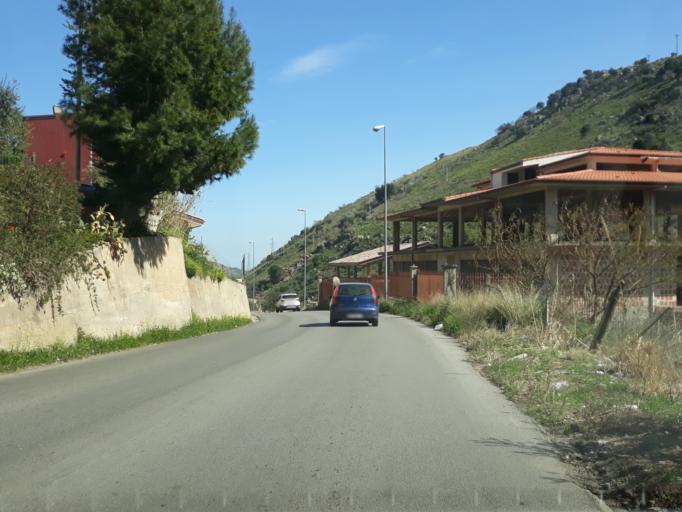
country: IT
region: Sicily
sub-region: Palermo
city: Belmonte Mezzagno
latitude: 38.0468
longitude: 13.3987
